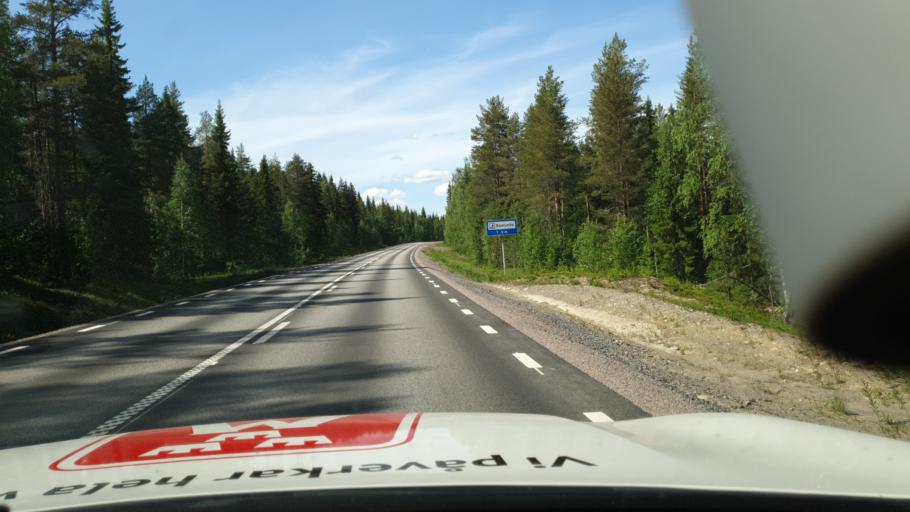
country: SE
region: Vaesterbotten
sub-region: Skelleftea Kommun
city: Boliden
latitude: 64.8858
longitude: 20.3835
